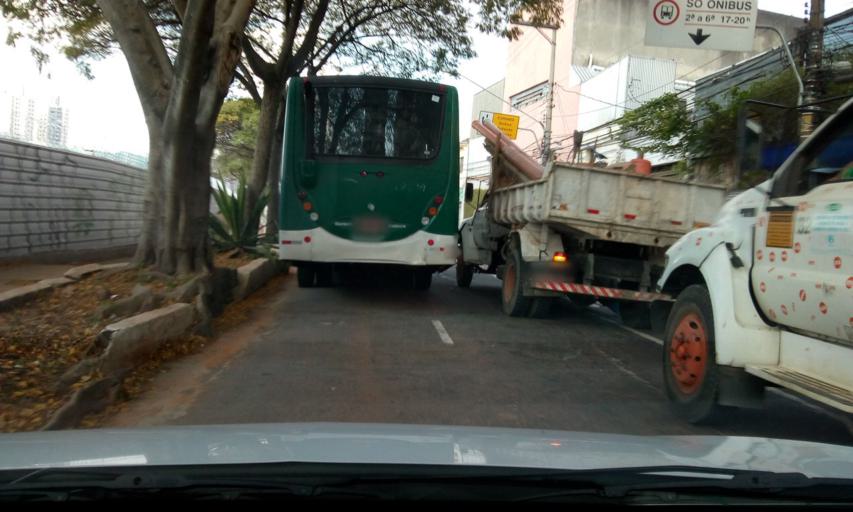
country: BR
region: Sao Paulo
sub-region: Sao Paulo
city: Sao Paulo
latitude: -23.5617
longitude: -46.6279
